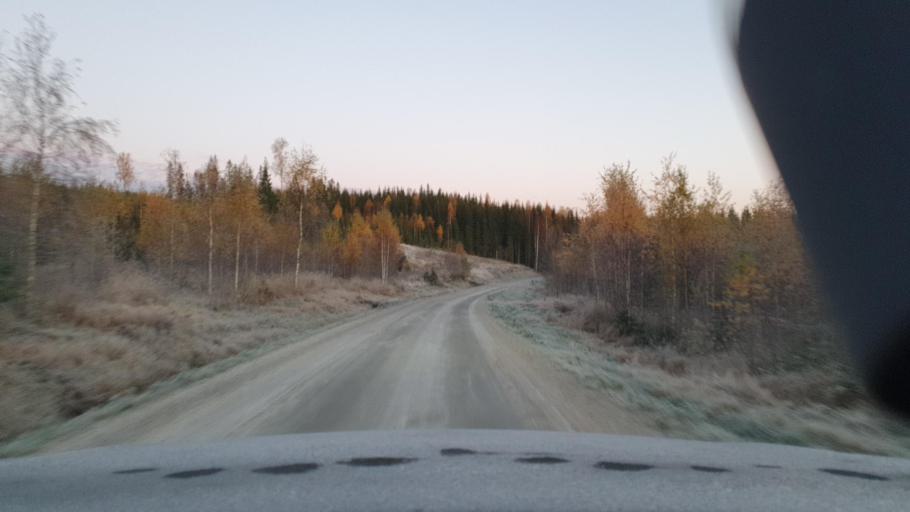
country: SE
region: Vaermland
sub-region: Arvika Kommun
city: Arvika
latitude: 59.7943
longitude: 12.7523
